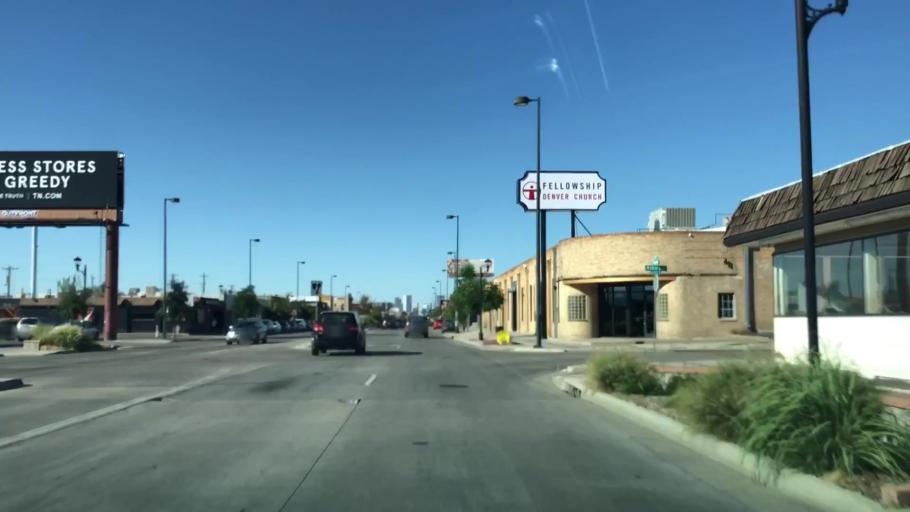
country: US
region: Colorado
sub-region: Arapahoe County
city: Englewood
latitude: 39.6801
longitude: -104.9875
